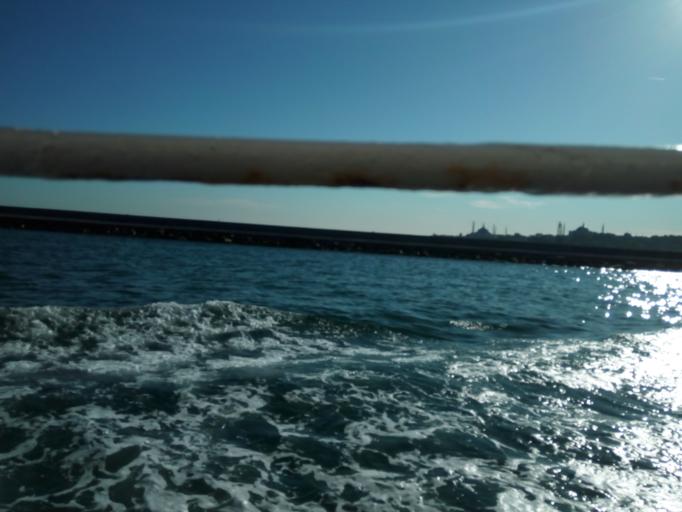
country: TR
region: Istanbul
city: UEskuedar
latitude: 41.0090
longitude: 29.0032
